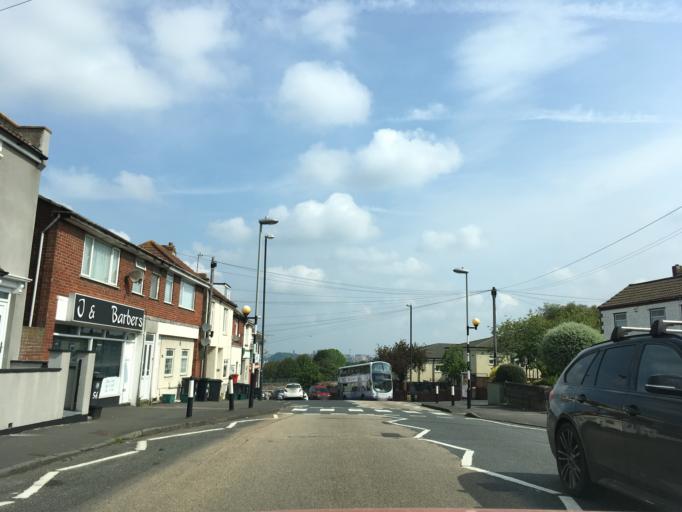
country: GB
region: England
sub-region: Bristol
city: Bristol
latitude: 51.4270
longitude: -2.6137
